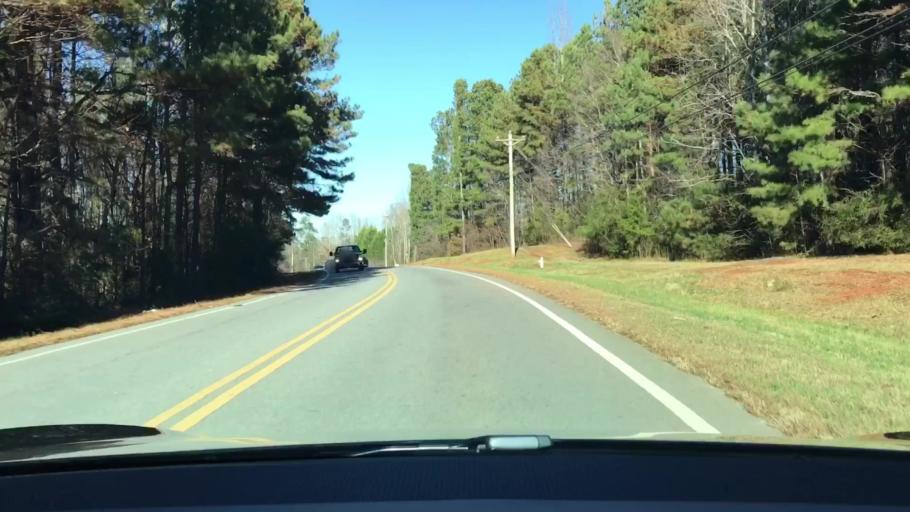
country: US
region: Georgia
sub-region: Barrow County
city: Auburn
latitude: 34.0916
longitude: -83.8695
